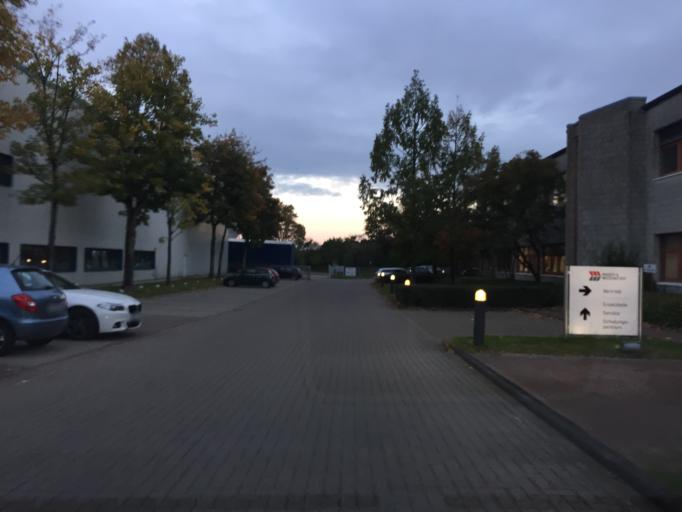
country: DE
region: Lower Saxony
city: Oyten
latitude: 53.0573
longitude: 9.0339
